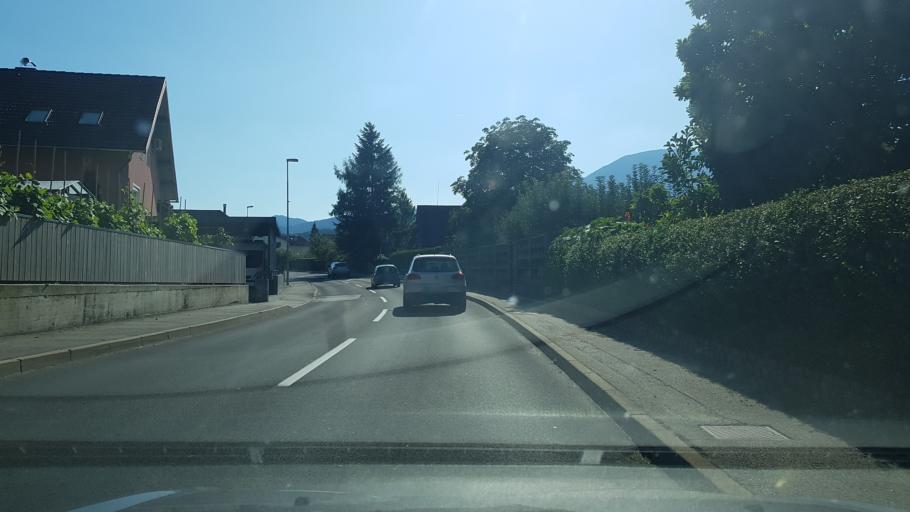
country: SI
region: Slovenj Gradec
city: Slovenj Gradec
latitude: 46.5057
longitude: 15.0758
